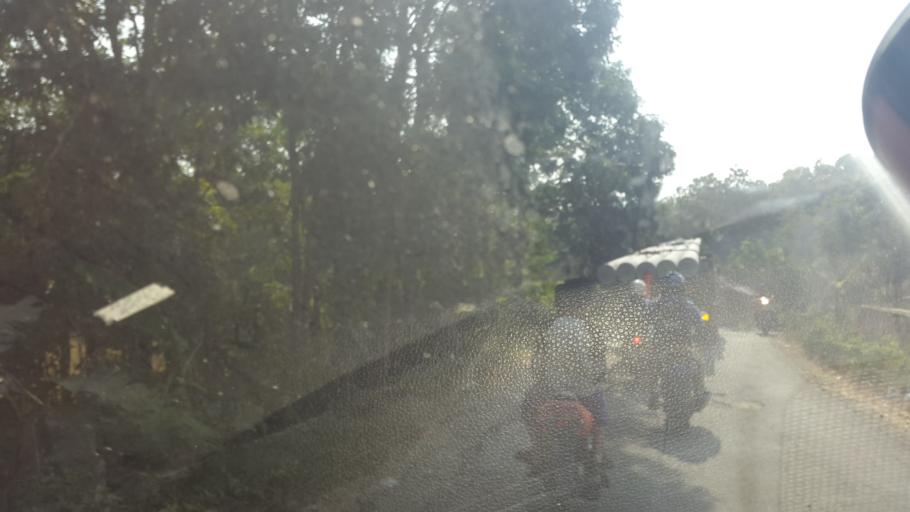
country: ID
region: West Java
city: Cimanggu
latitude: -7.2496
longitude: 106.6607
